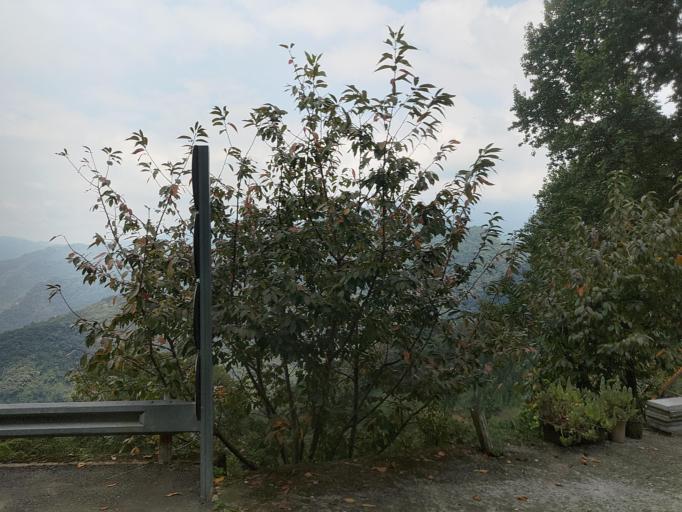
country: TW
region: Taiwan
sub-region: Hsinchu
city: Hsinchu
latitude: 24.6106
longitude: 121.0991
